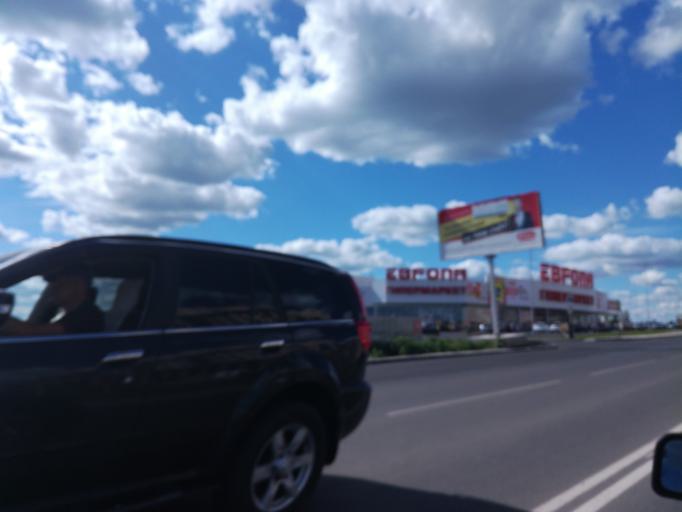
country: RU
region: Kursk
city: Kursk
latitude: 51.8033
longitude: 36.1642
